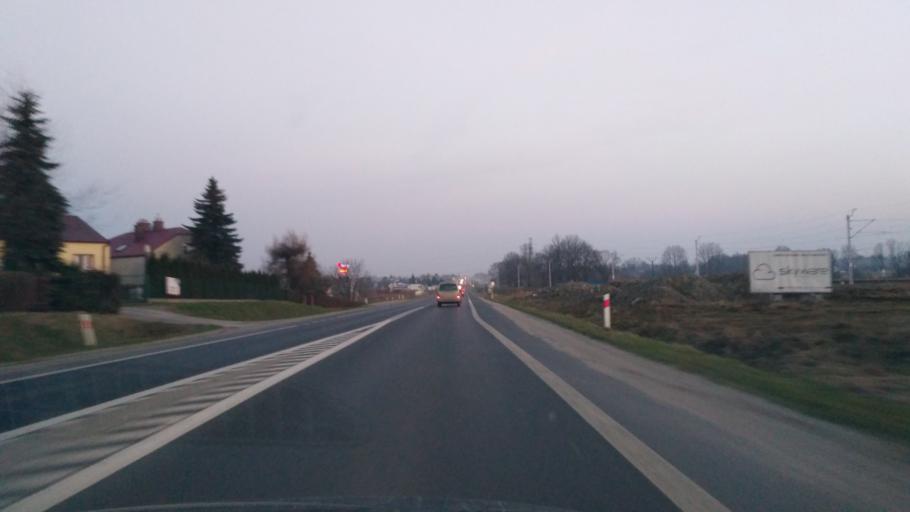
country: PL
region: Subcarpathian Voivodeship
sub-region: Powiat rzeszowski
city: Rudna Mala
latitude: 50.0951
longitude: 21.9802
